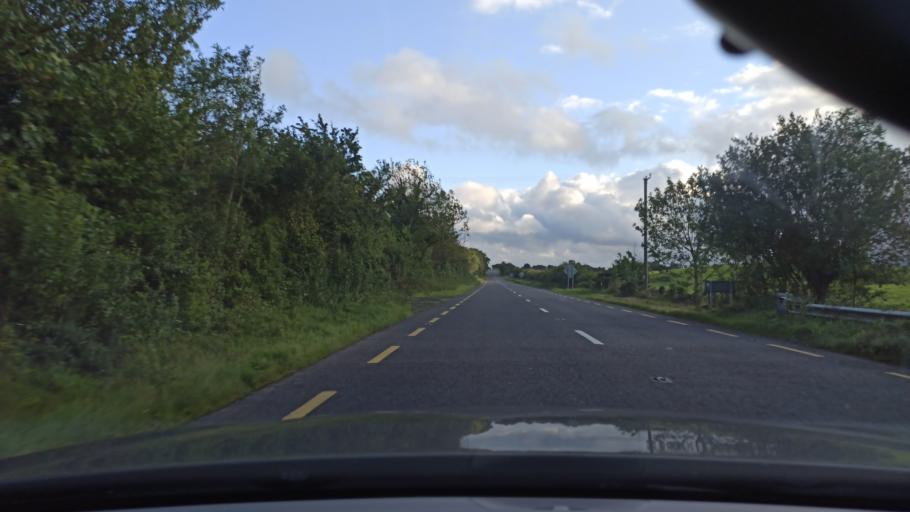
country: IE
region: Munster
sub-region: North Tipperary
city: Roscrea
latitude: 52.8838
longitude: -7.8053
